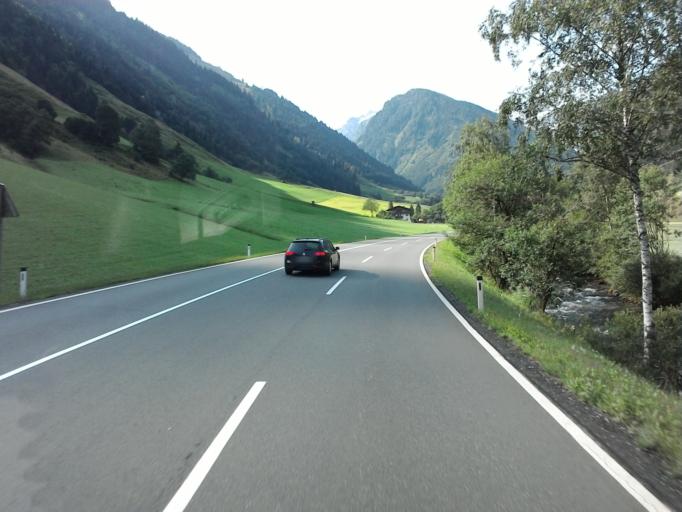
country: AT
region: Salzburg
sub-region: Politischer Bezirk Zell am See
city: Mittersill
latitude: 47.2437
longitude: 12.4912
